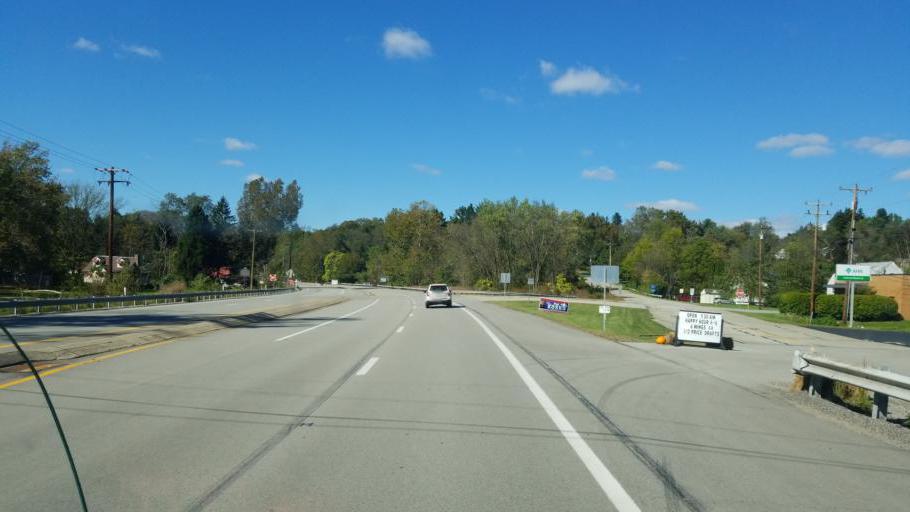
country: US
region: Pennsylvania
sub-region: Westmoreland County
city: Ligonier
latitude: 40.2366
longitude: -79.2295
